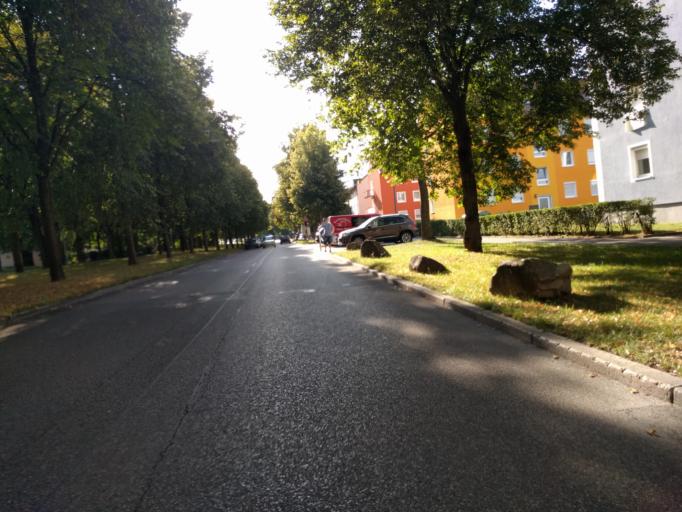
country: DE
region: Bavaria
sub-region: Upper Palatinate
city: Regensburg
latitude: 49.0016
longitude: 12.1175
